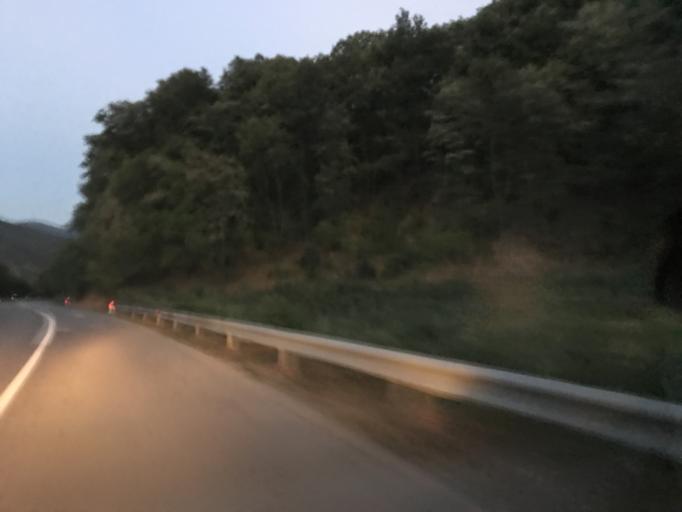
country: RO
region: Caras-Severin
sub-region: Comuna Berzasca
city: Berzasca
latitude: 44.6293
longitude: 21.9854
